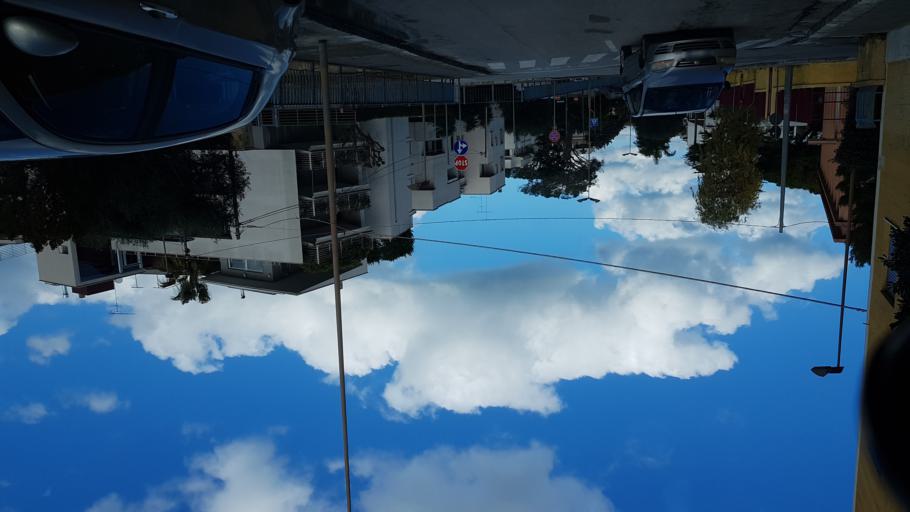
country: IT
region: Apulia
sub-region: Provincia di Brindisi
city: Brindisi
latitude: 40.6449
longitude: 17.9409
